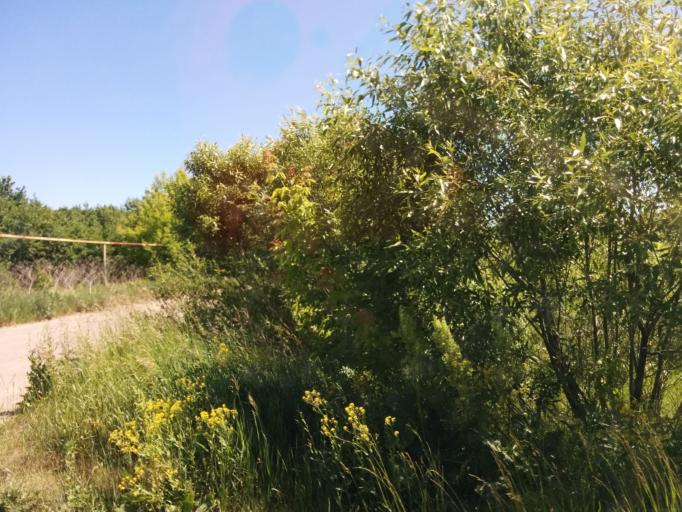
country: RU
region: Tambov
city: Morshansk
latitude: 53.6153
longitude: 41.8442
